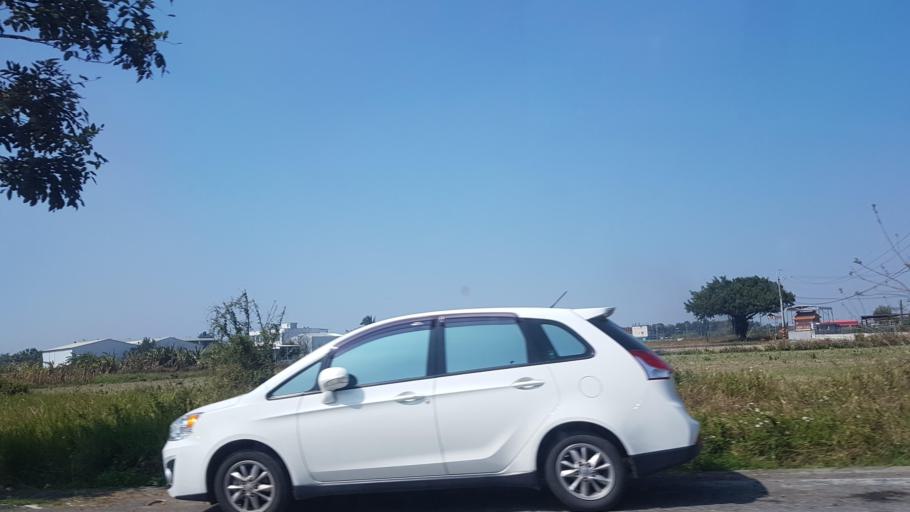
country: TW
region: Taiwan
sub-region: Tainan
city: Tainan
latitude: 22.9337
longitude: 120.2605
